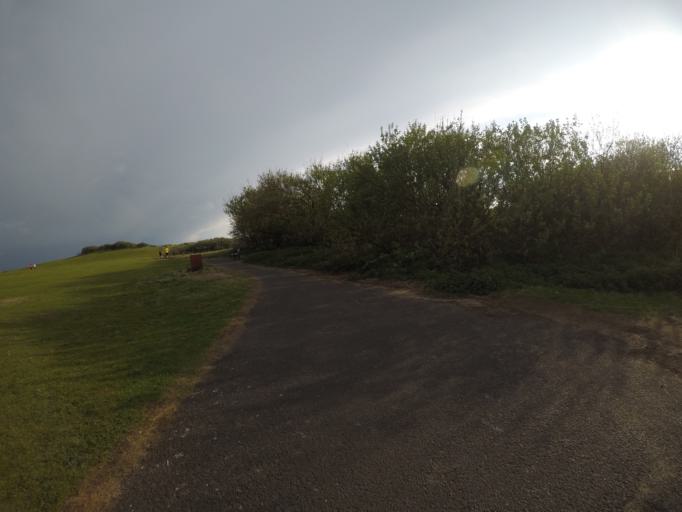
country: GB
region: Scotland
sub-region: North Ayrshire
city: Irvine
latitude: 55.6048
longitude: -4.6911
